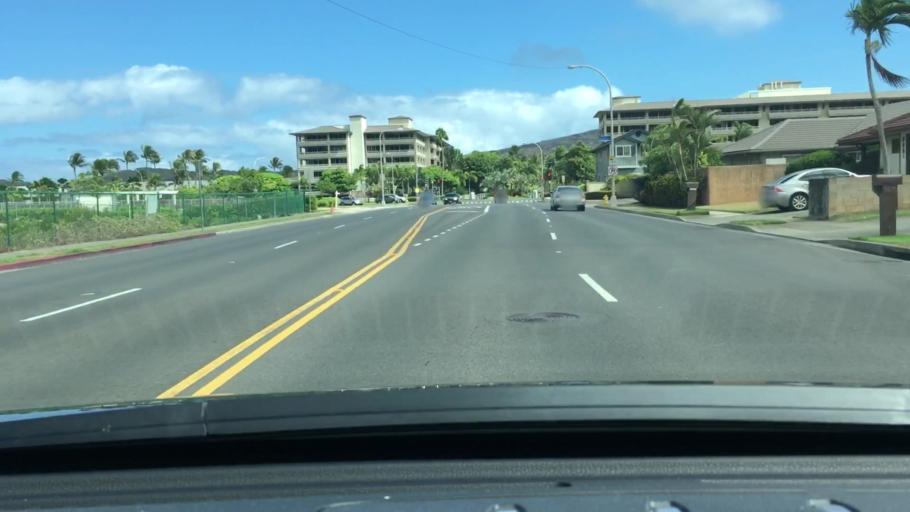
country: US
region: Hawaii
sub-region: Honolulu County
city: Waimanalo Beach
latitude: 21.2880
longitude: -157.7064
